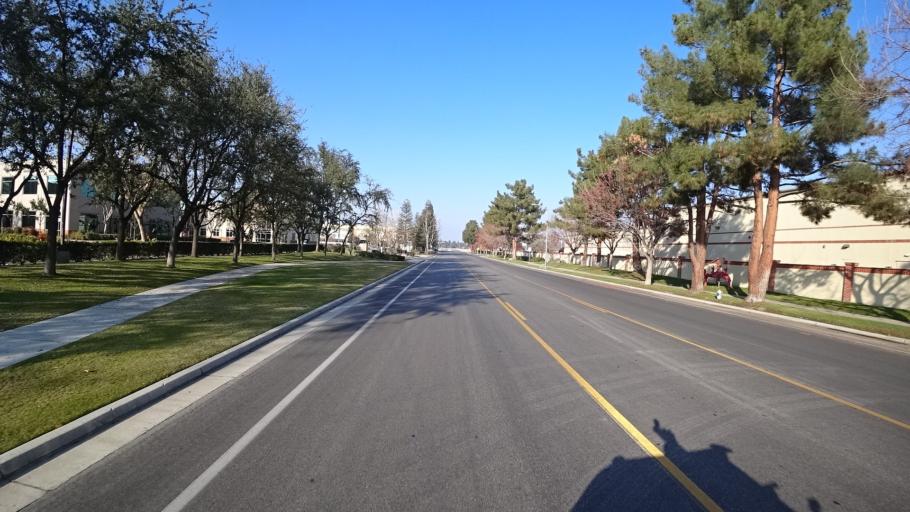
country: US
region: California
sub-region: Kern County
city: Greenacres
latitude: 35.3407
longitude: -119.1062
